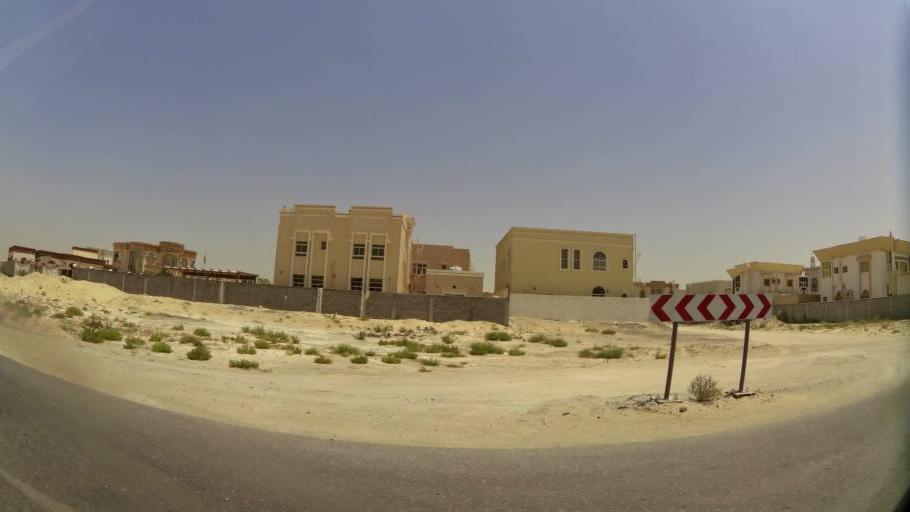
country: AE
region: Ajman
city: Ajman
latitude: 25.4037
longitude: 55.5227
